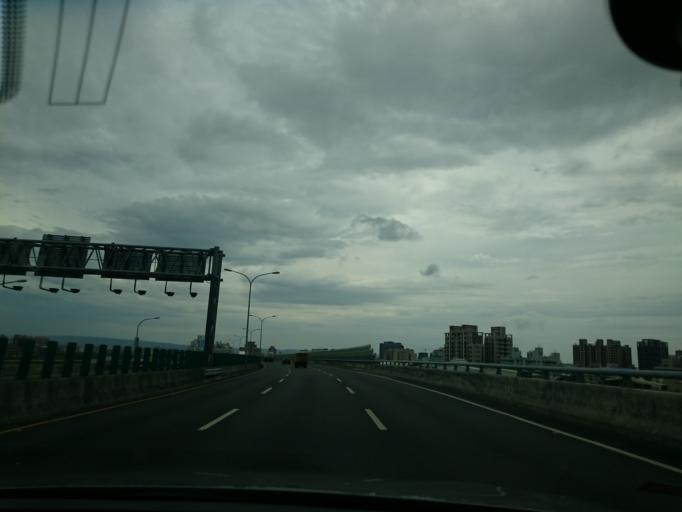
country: TW
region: Taiwan
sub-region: Taichung City
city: Taichung
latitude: 24.1119
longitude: 120.6974
